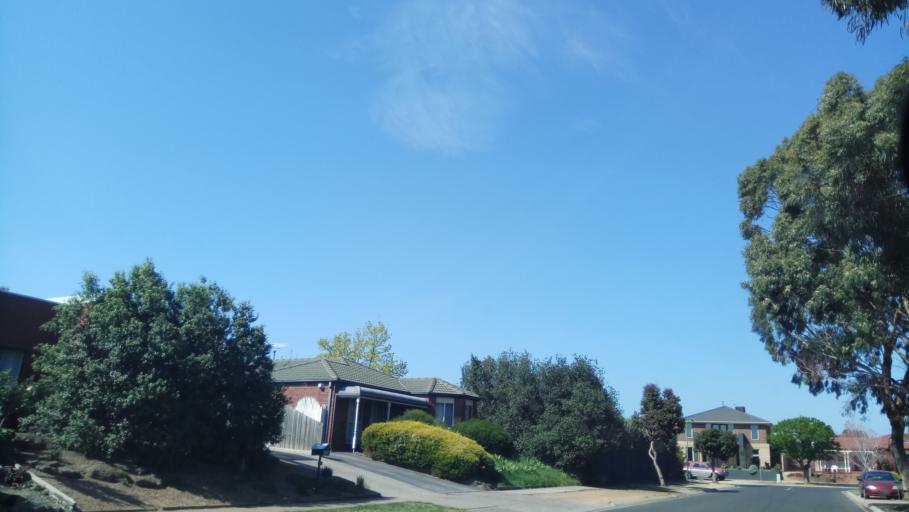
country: AU
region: Victoria
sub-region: Hobsons Bay
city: Altona Meadows
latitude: -37.8851
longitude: 144.7606
